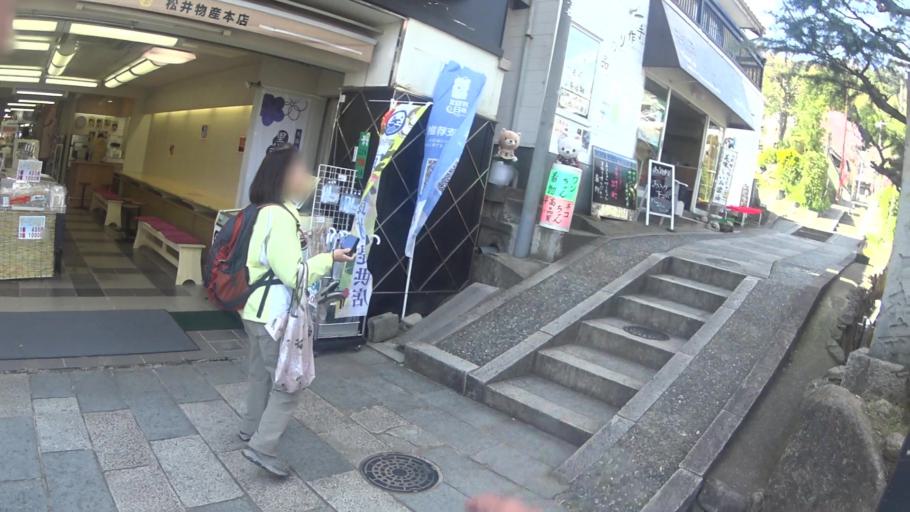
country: JP
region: Kyoto
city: Miyazu
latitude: 35.5831
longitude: 135.1951
